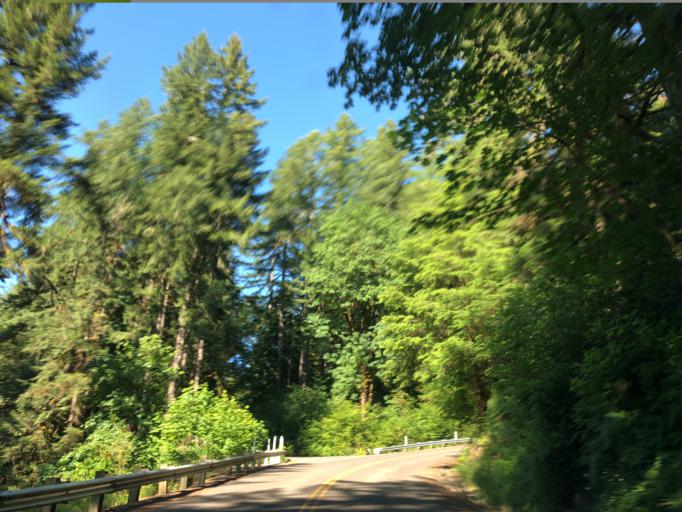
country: US
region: Oregon
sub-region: Linn County
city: Sweet Home
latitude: 44.4665
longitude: -122.6755
